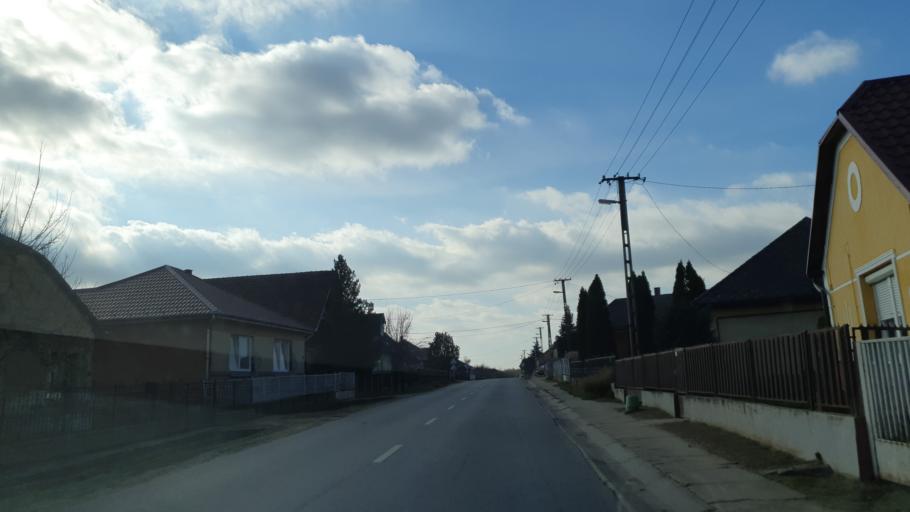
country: HU
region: Szabolcs-Szatmar-Bereg
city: Nyirkarasz
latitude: 48.0954
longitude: 22.0985
